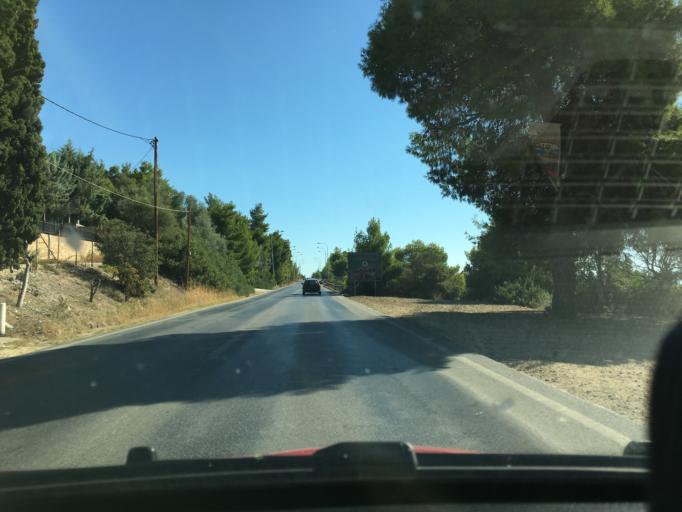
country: GR
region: Central Macedonia
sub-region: Nomos Chalkidikis
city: Ormylia
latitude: 40.2607
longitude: 23.4820
